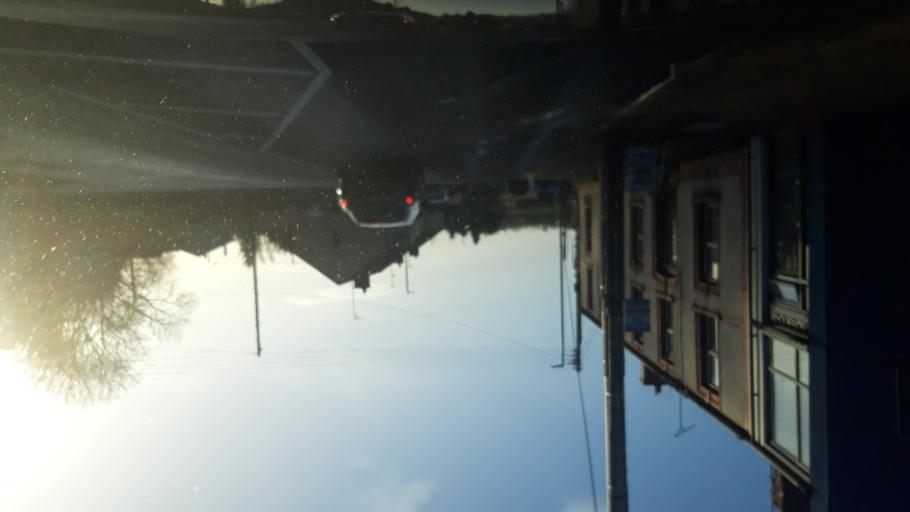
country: GB
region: Northern Ireland
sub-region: Magherafelt District
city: Magherafelt
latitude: 54.7701
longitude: -6.6728
